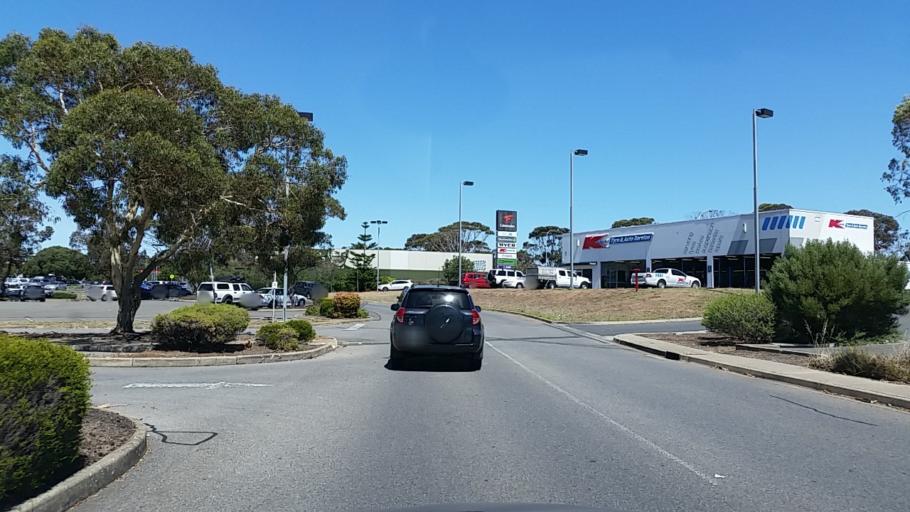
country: AU
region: South Australia
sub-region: Onkaparinga
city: Noarlunga Downs
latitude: -35.1431
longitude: 138.4943
